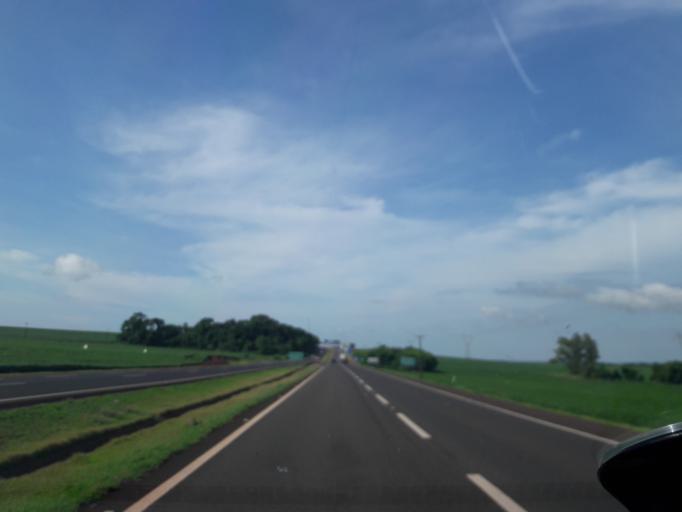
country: BR
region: Parana
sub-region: Paicandu
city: Paicandu
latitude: -23.6298
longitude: -52.1022
